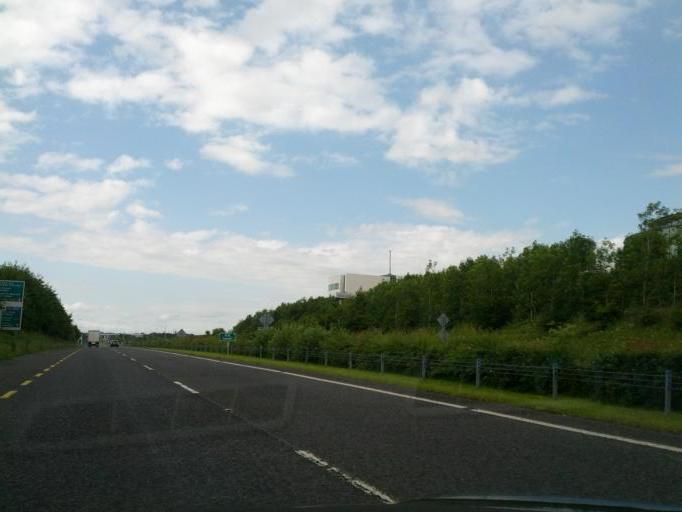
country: IE
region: Connaught
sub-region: County Galway
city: Oranmore
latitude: 53.2807
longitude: -8.9745
